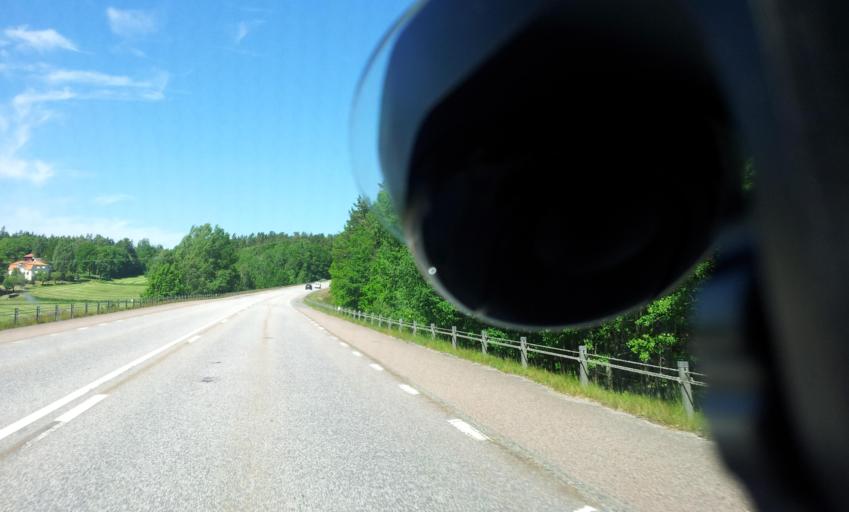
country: SE
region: Kalmar
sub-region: Vasterviks Kommun
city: Ankarsrum
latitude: 57.6637
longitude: 16.4435
